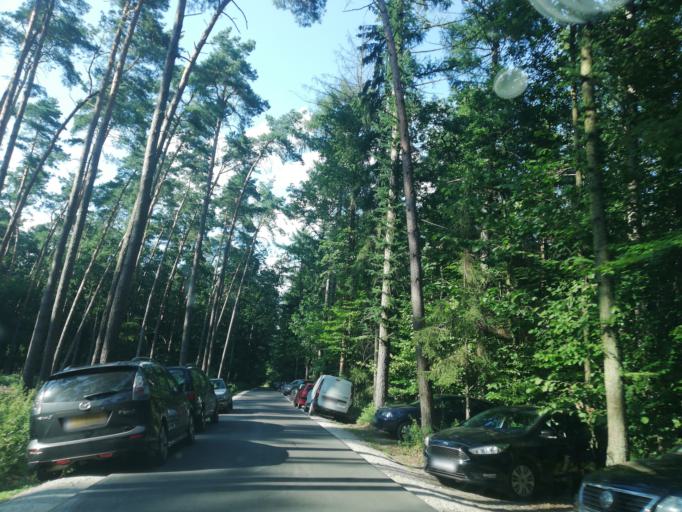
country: PL
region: Kujawsko-Pomorskie
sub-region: Powiat golubsko-dobrzynski
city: Ciechocin
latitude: 53.0775
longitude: 18.9500
